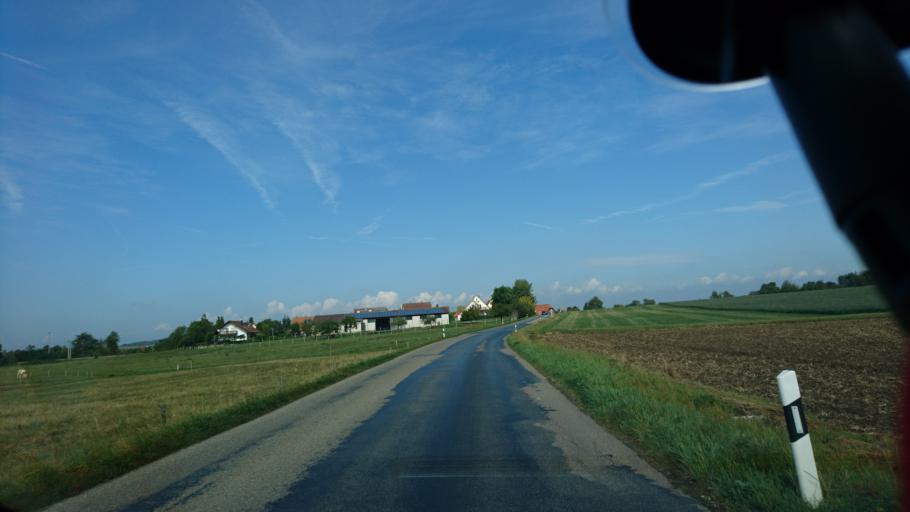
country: DE
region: Baden-Wuerttemberg
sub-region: Regierungsbezirk Stuttgart
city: Ilshofen
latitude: 49.1407
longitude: 9.9262
